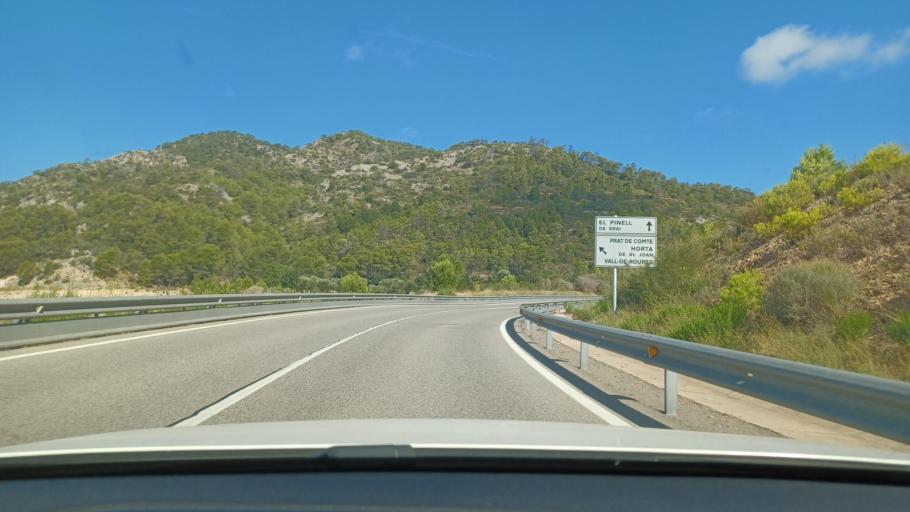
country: ES
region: Catalonia
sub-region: Provincia de Tarragona
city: Benifallet
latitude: 40.9718
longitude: 0.4459
